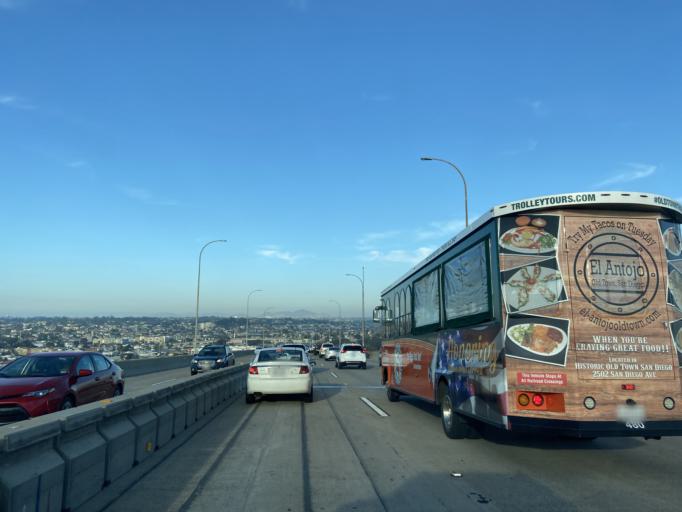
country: US
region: California
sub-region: San Diego County
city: San Diego
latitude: 32.6923
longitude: -117.1500
